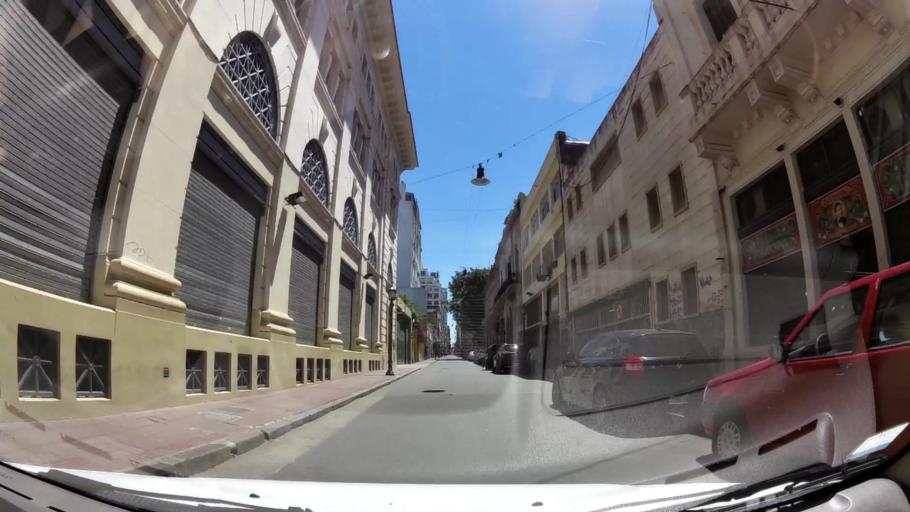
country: AR
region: Buenos Aires F.D.
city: Buenos Aires
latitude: -34.6146
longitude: -58.3718
